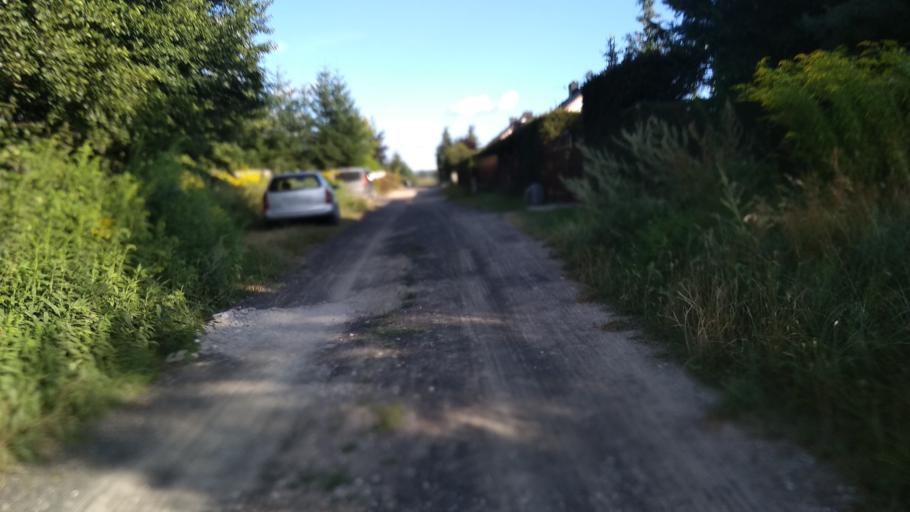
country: PL
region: Kujawsko-Pomorskie
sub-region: Powiat bydgoski
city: Osielsko
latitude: 53.2306
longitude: 18.1218
